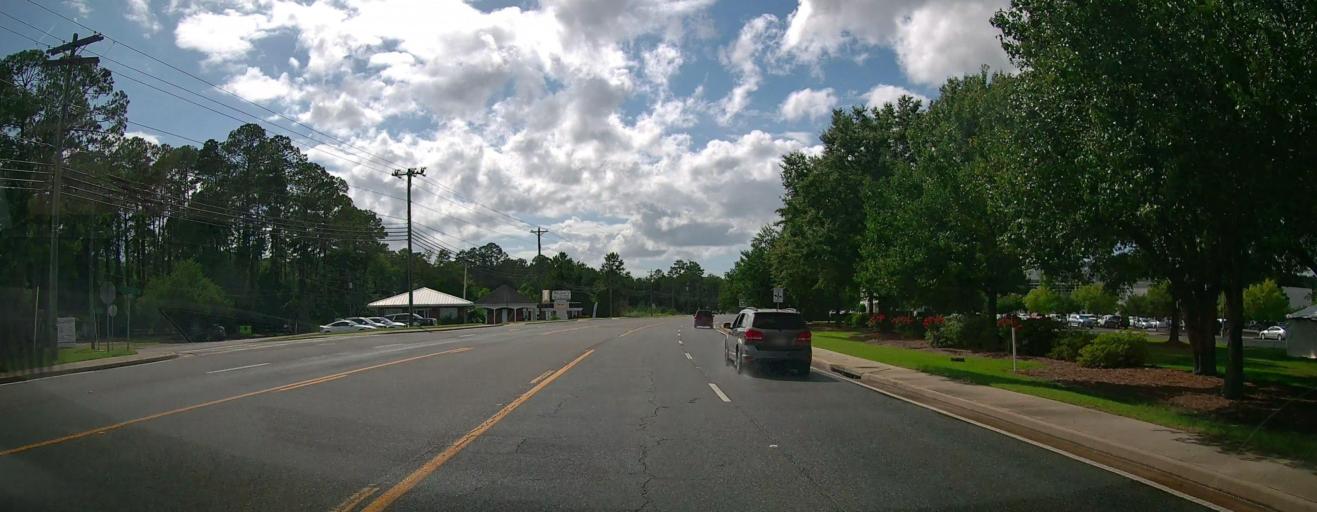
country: US
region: Georgia
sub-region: Coffee County
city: Douglas
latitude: 31.5095
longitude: -82.8628
